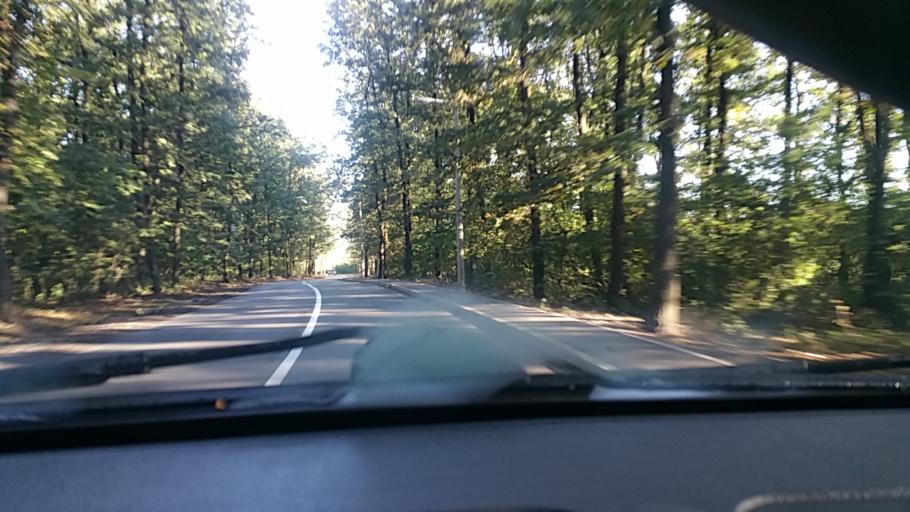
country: RS
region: Central Serbia
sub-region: Belgrade
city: Rakovica
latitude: 44.7395
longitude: 20.4633
